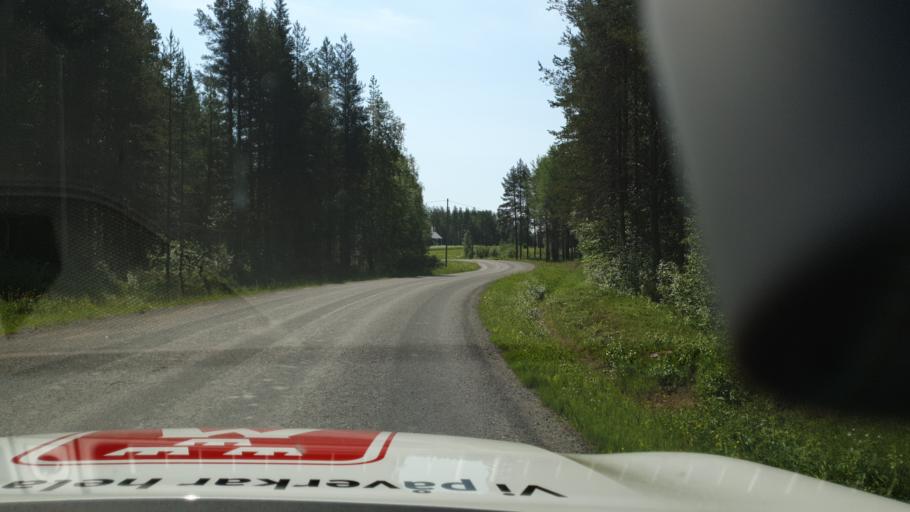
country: SE
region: Vaesterbotten
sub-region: Skelleftea Kommun
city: Langsele
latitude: 65.0145
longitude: 20.0793
